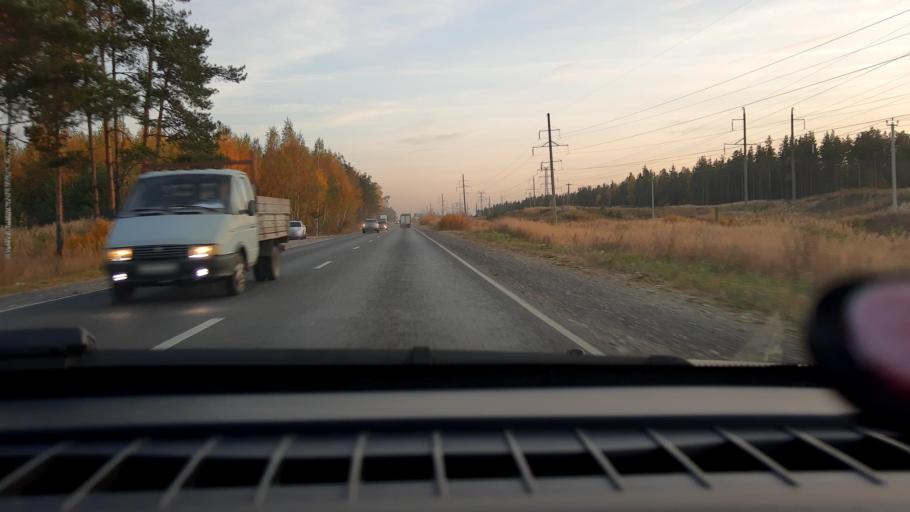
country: RU
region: Nizjnij Novgorod
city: Babino
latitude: 56.3123
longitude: 43.5591
